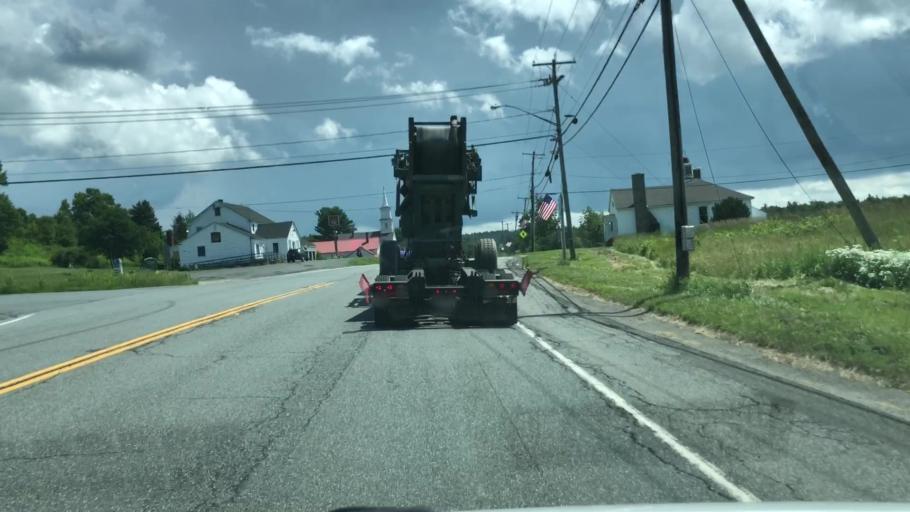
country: US
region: Massachusetts
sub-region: Berkshire County
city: Hinsdale
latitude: 42.5115
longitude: -73.0586
